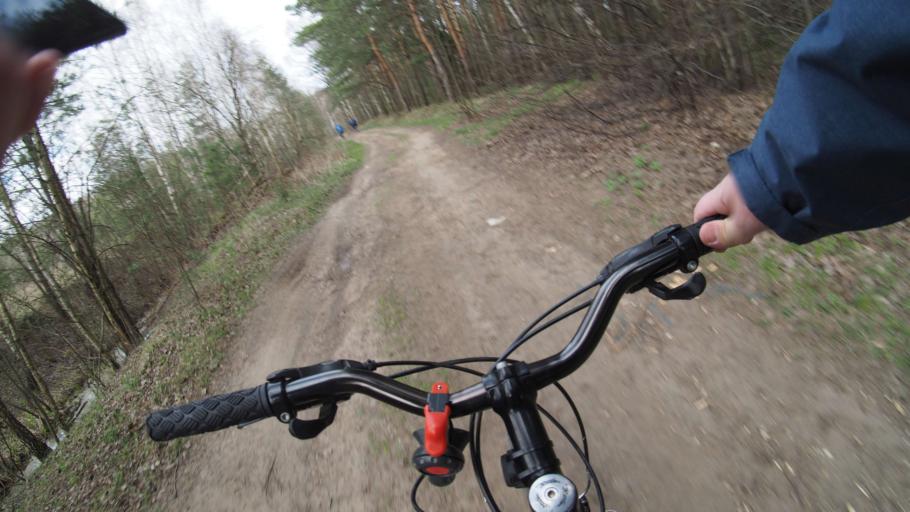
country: RU
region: Moskovskaya
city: Ramenskoye
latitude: 55.5927
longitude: 38.2910
